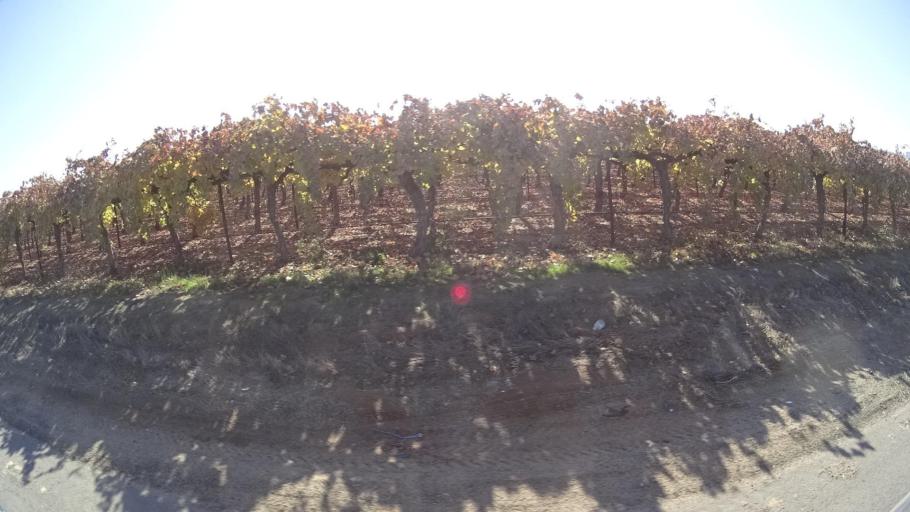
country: US
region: California
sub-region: Tulare County
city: Richgrove
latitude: 35.7180
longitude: -119.1488
